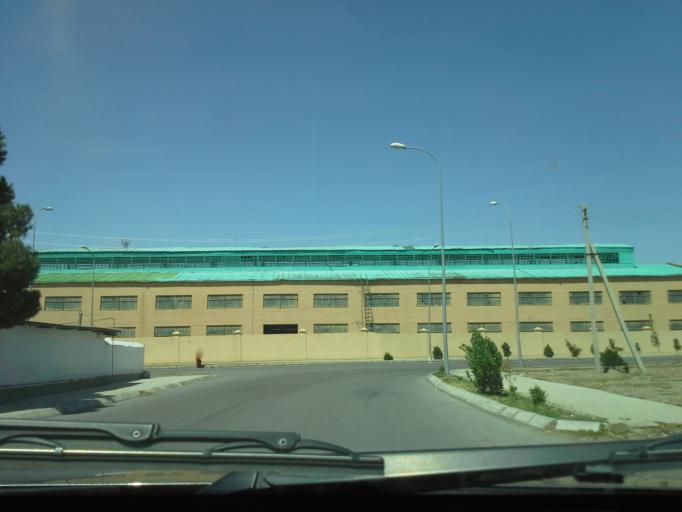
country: TM
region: Balkan
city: Serdar
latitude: 38.9767
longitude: 56.2737
